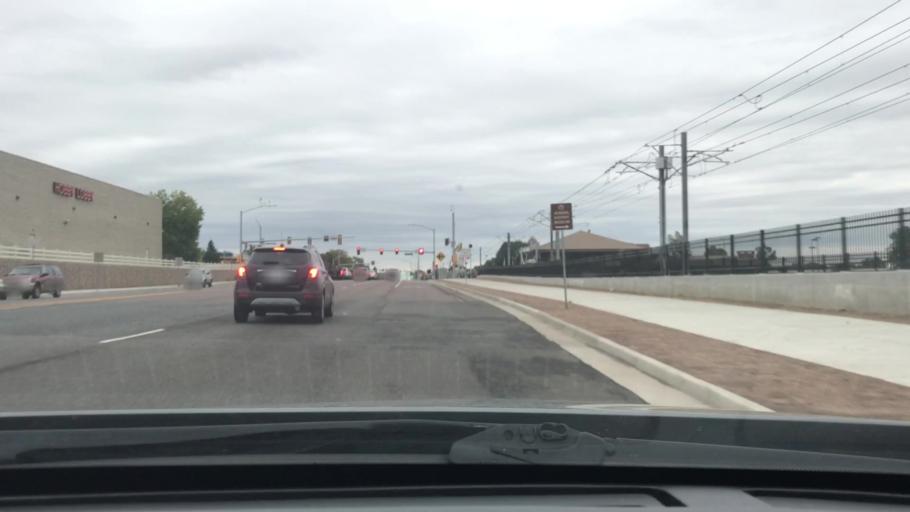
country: US
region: Colorado
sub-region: Adams County
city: Aurora
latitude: 39.7096
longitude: -104.8192
